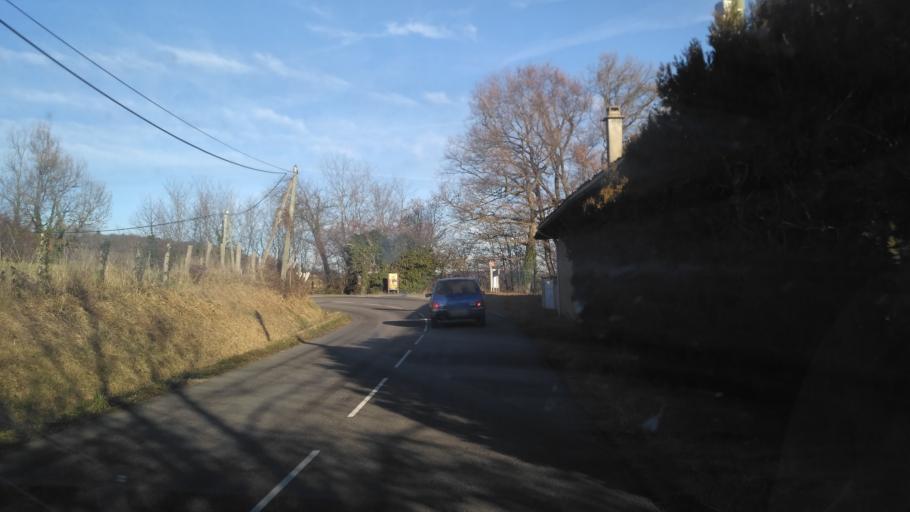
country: FR
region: Rhone-Alpes
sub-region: Departement de l'Isere
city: Saint-Antoine-l'Abbaye
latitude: 45.1658
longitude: 5.2022
